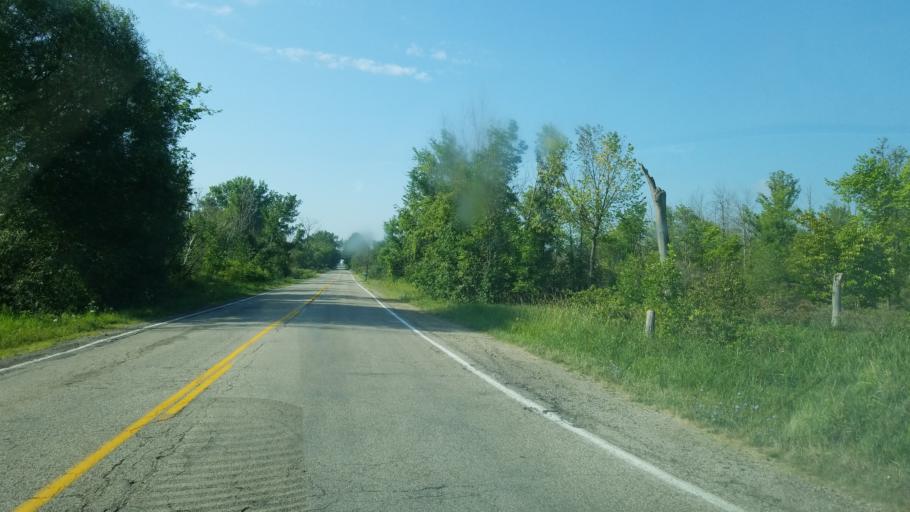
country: US
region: Michigan
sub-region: Kent County
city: Cedar Springs
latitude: 43.2941
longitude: -85.5518
